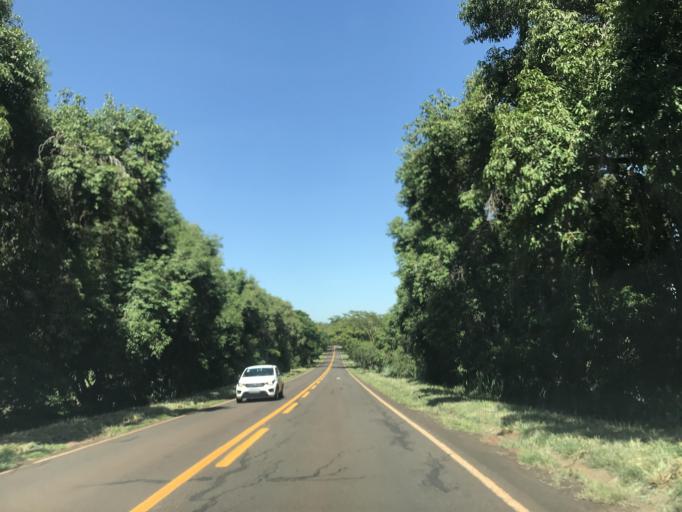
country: BR
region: Parana
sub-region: Terra Rica
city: Terra Rica
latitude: -22.7734
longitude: -52.6501
